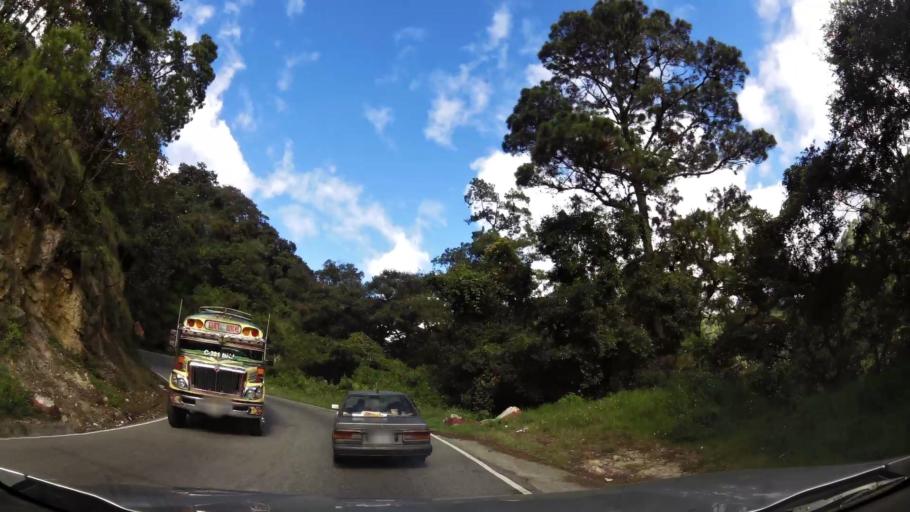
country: GT
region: Quiche
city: Chichicastenango
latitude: 14.9201
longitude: -91.1051
